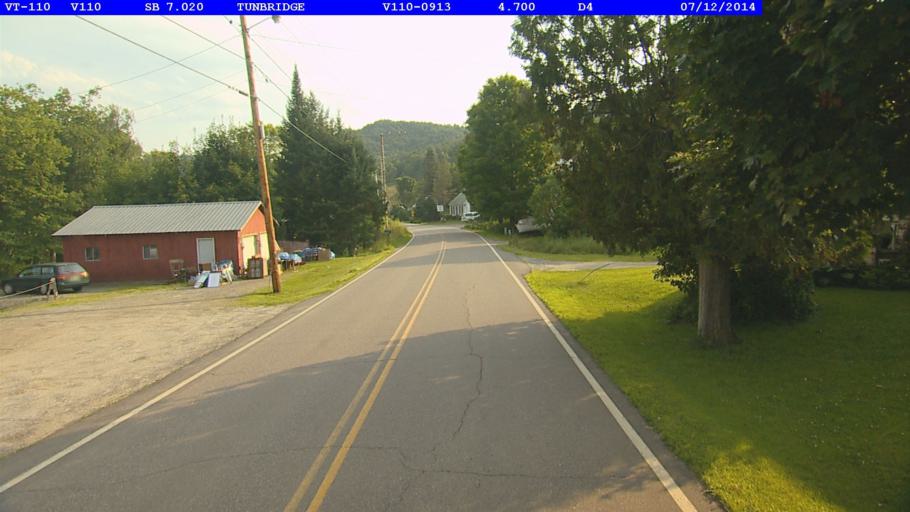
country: US
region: Vermont
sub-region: Orange County
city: Chelsea
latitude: 43.9120
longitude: -72.4818
